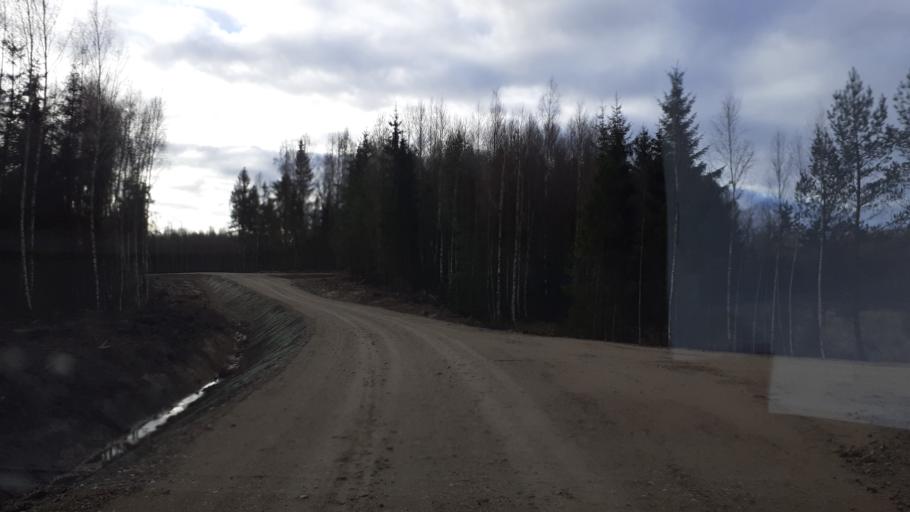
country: LV
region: Skrunda
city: Skrunda
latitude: 56.7893
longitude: 21.8353
